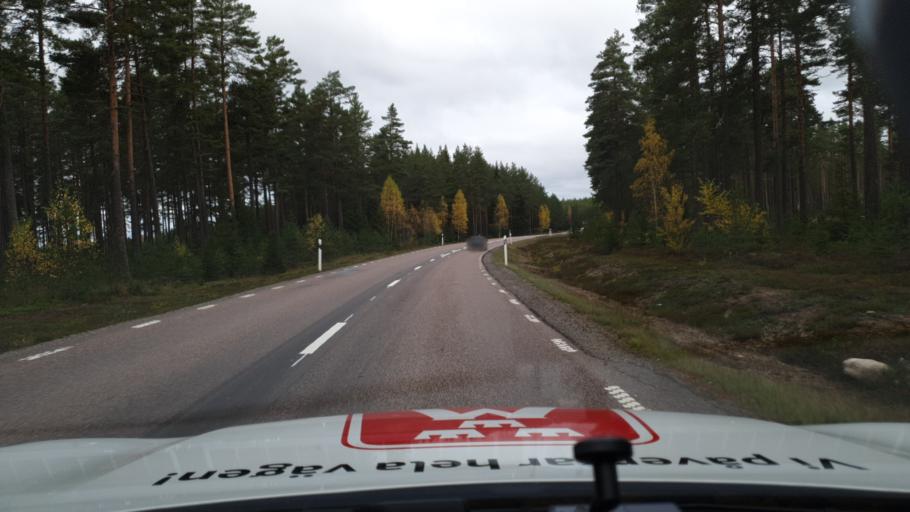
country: SE
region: Gaevleborg
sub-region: Gavle Kommun
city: Hedesunda
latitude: 60.4475
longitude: 16.9608
